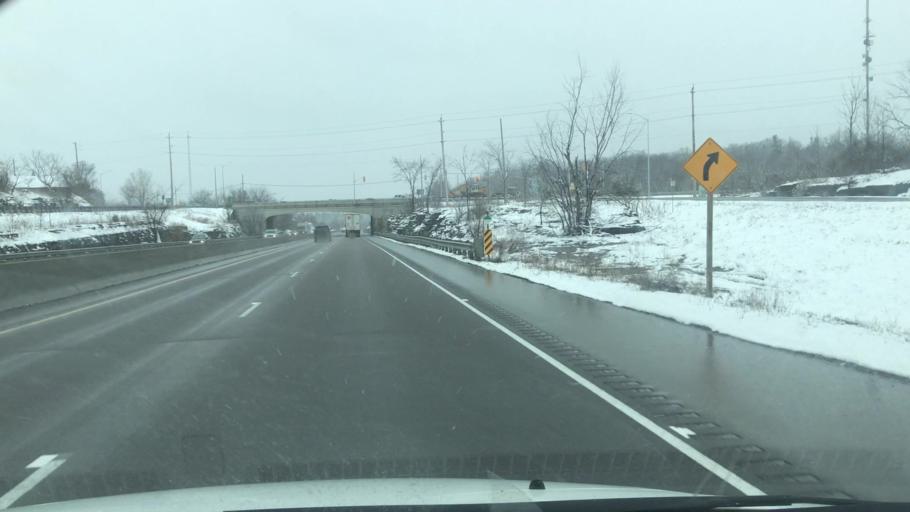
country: CA
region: Ontario
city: Kingston
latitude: 44.2903
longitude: -76.4275
